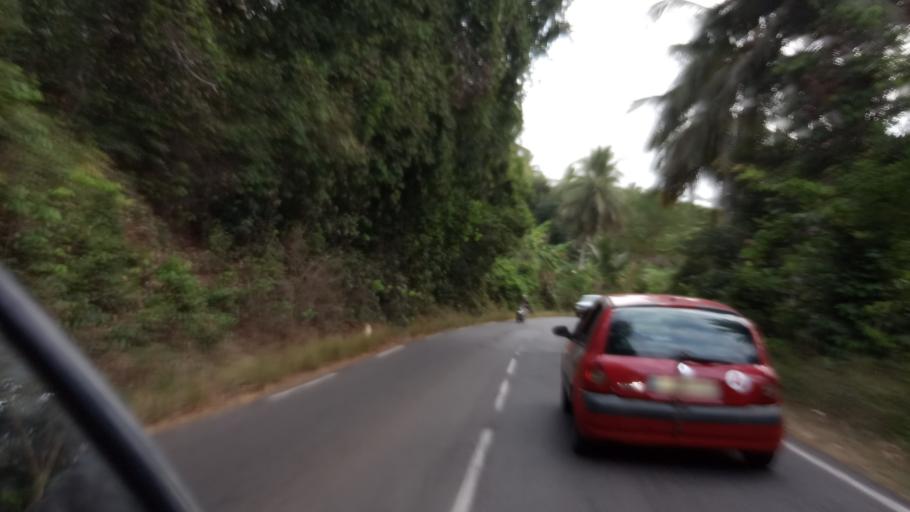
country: YT
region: Dembeni
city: Dembeni
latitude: -12.8322
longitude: 45.1919
